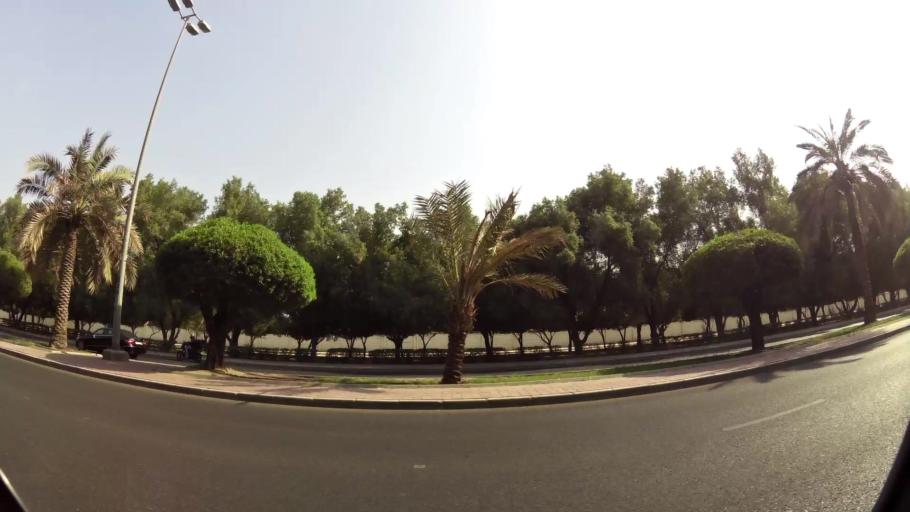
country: KW
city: Bayan
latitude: 29.3024
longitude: 48.0578
